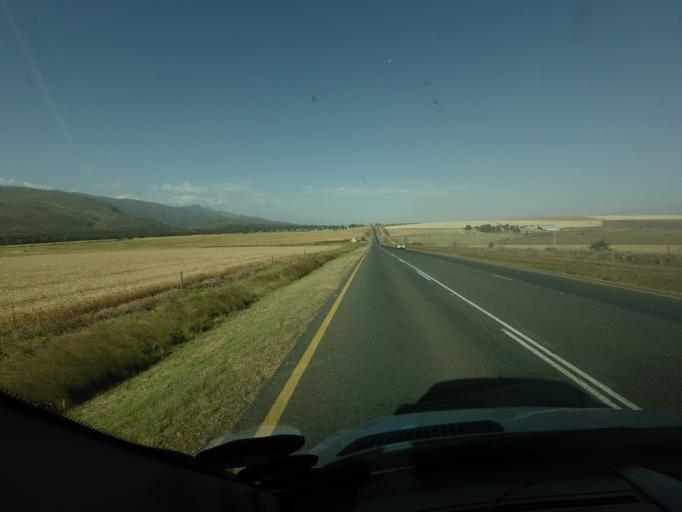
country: ZA
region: Western Cape
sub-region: Cape Winelands District Municipality
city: Ashton
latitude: -34.1555
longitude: 19.8825
